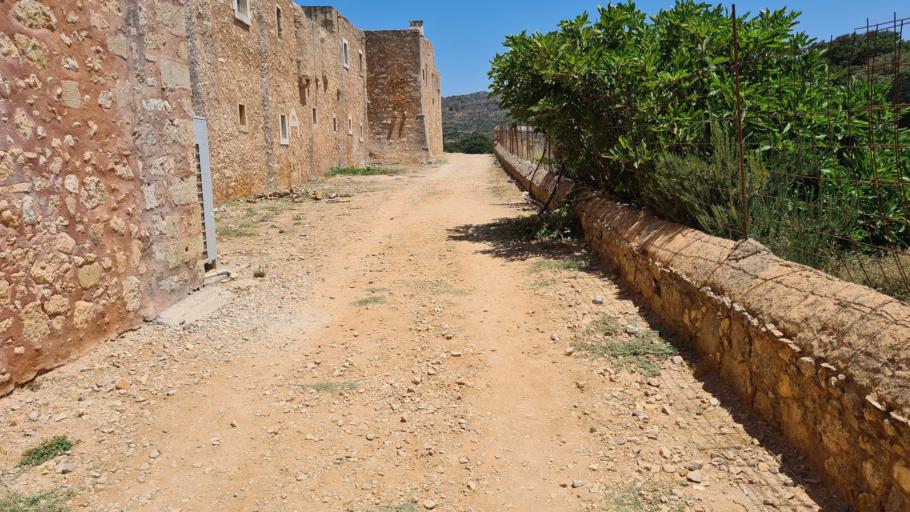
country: GR
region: Crete
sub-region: Nomos Rethymnis
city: Agia Foteini
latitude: 35.3096
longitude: 24.6292
